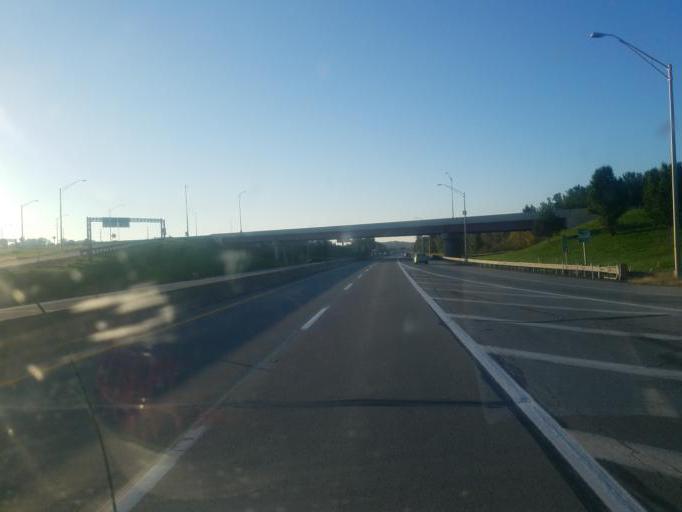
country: US
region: Pennsylvania
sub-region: Butler County
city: Cranberry Township
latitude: 40.6801
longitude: -80.1049
